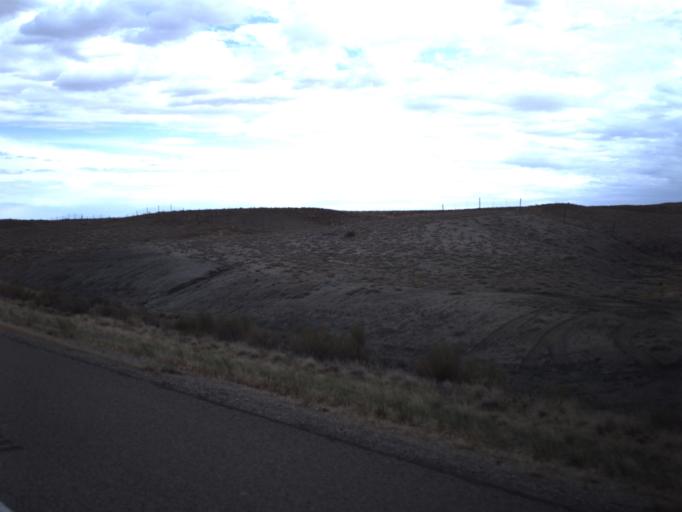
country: US
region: Utah
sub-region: Grand County
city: Moab
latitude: 38.9618
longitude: -110.0678
